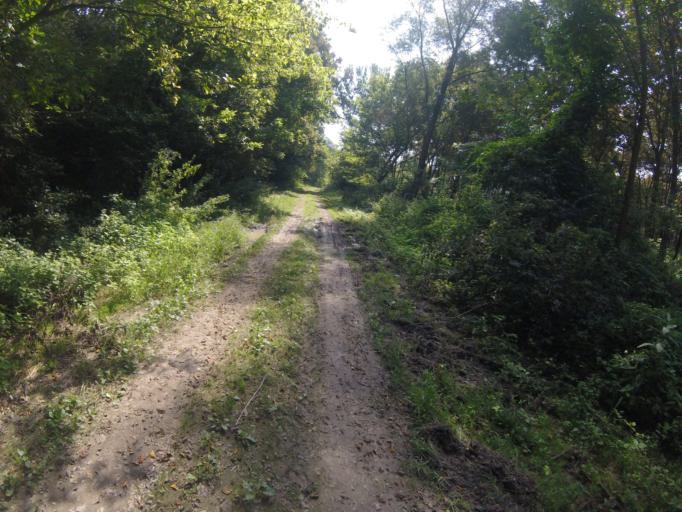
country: HU
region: Bacs-Kiskun
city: Baja
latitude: 46.2064
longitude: 18.8936
